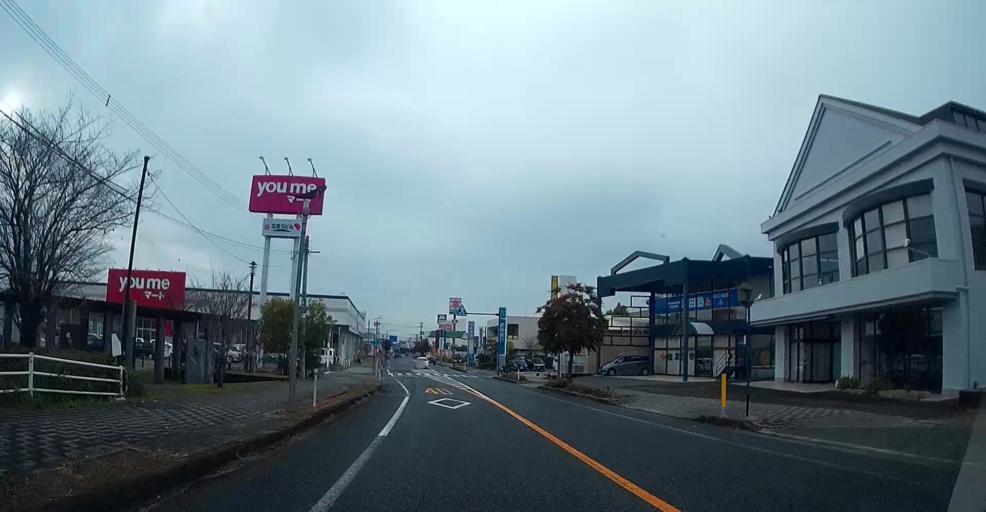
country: JP
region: Kumamoto
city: Matsubase
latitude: 32.6541
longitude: 130.6780
